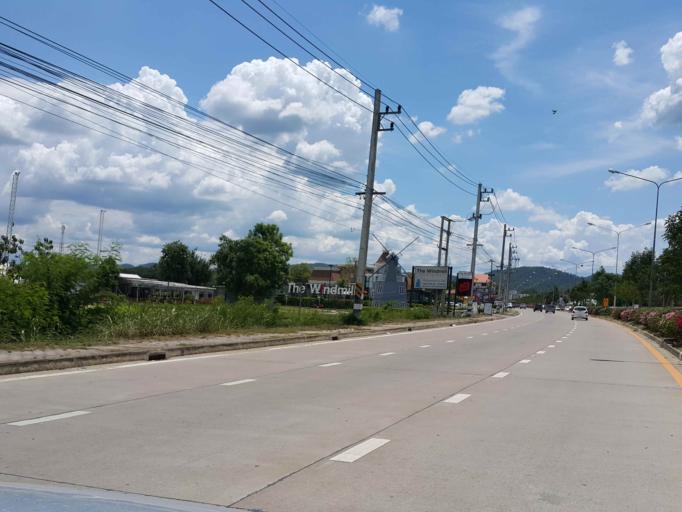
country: TH
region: Chiang Mai
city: Chiang Mai
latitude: 18.7479
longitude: 98.9495
